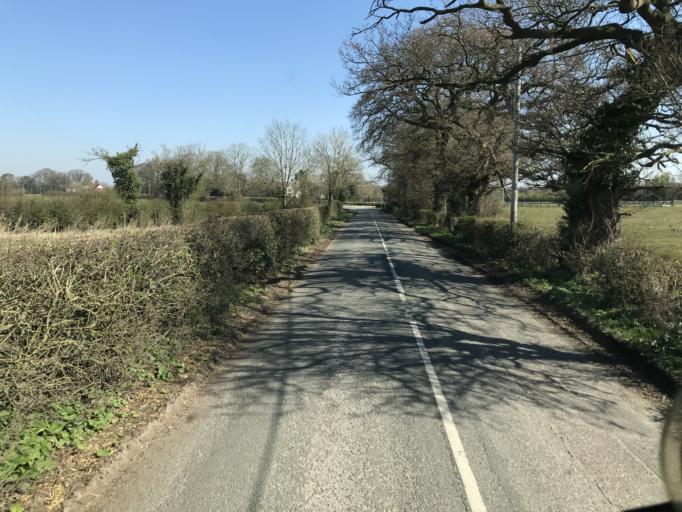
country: GB
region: England
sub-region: Cheshire West and Chester
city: Aldford
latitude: 53.1360
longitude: -2.8448
